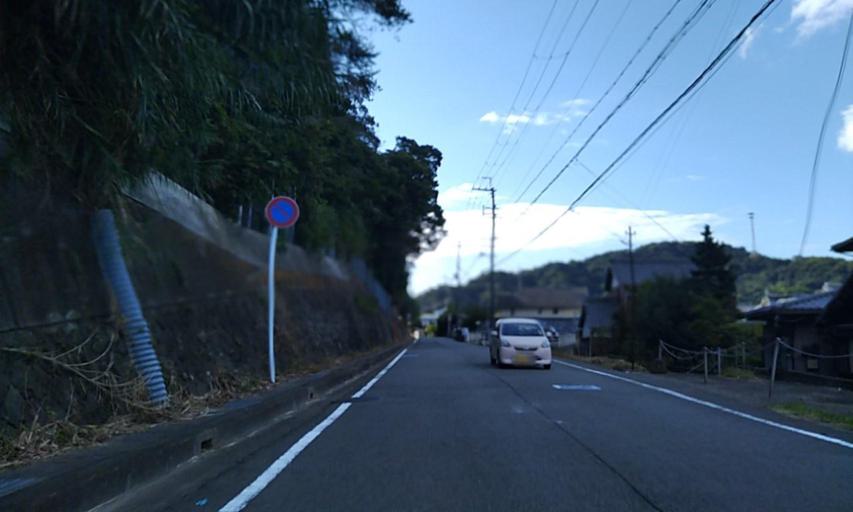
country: JP
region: Wakayama
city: Minato
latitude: 34.2785
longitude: 135.0757
